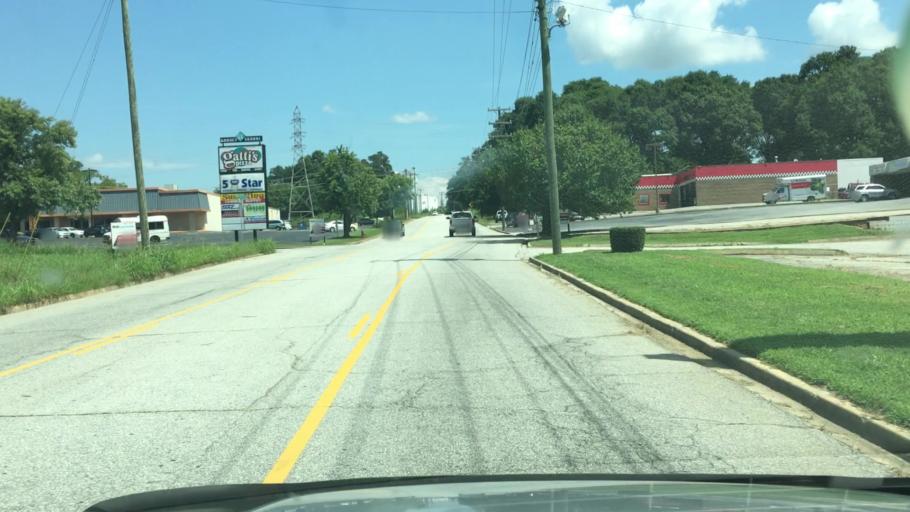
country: US
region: South Carolina
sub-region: Spartanburg County
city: Spartanburg
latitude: 34.9687
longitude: -81.9293
